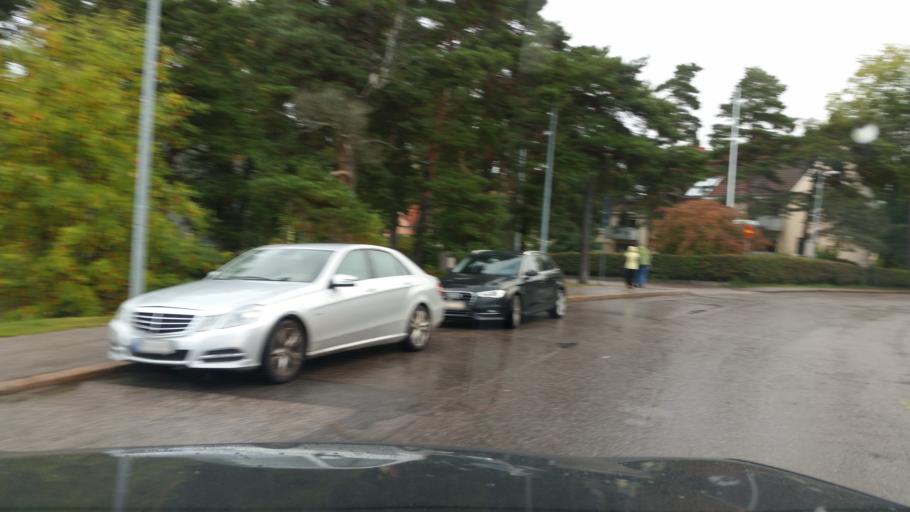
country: FI
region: Uusimaa
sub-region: Helsinki
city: Teekkarikylae
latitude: 60.1928
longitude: 24.8729
